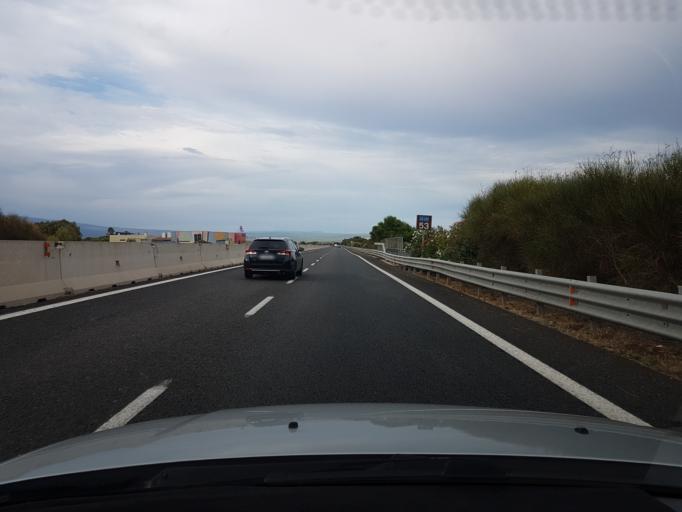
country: IT
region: Sardinia
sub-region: Provincia di Oristano
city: Siamaggiore
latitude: 39.9677
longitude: 8.6230
